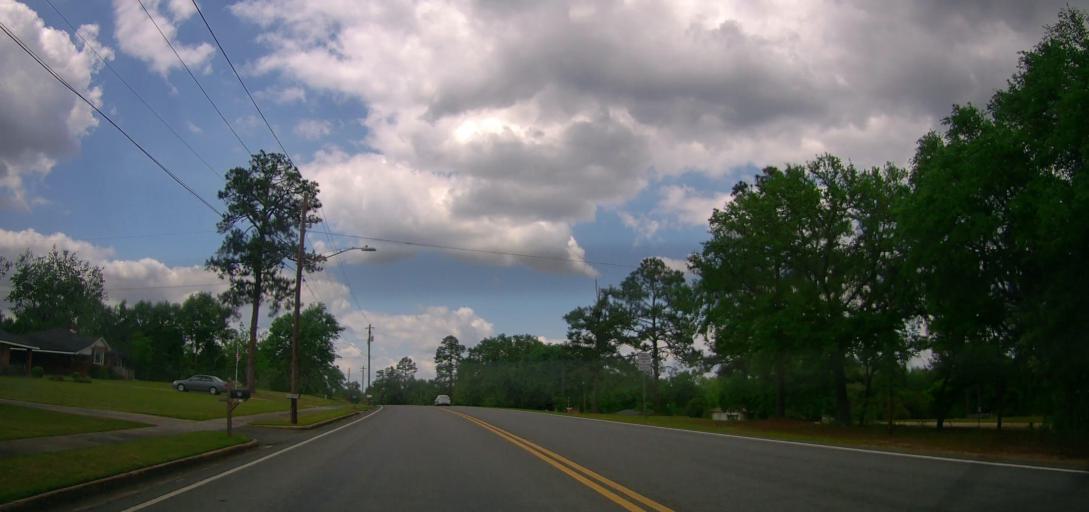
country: US
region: Georgia
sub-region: Treutlen County
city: Soperton
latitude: 32.3664
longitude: -82.5826
